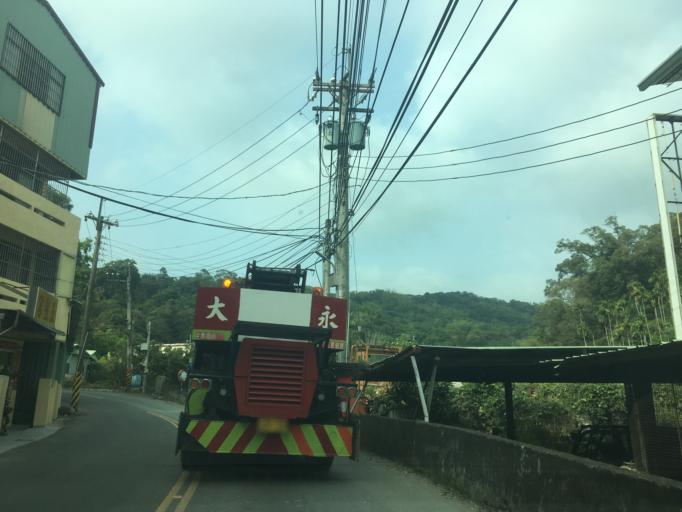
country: TW
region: Taiwan
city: Fengyuan
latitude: 24.2354
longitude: 120.7388
